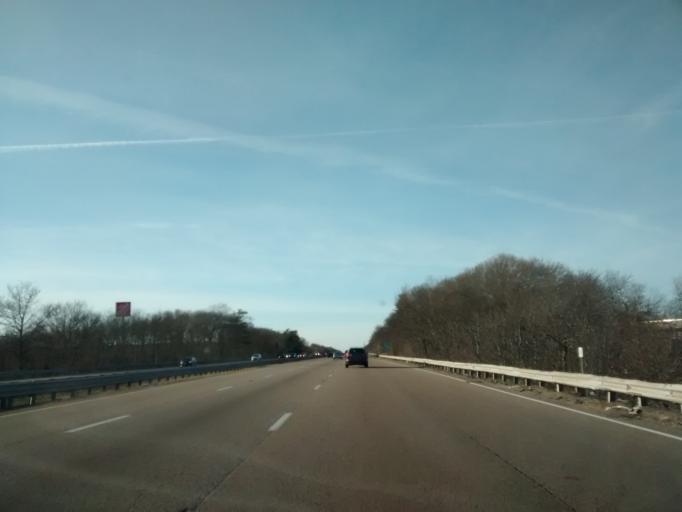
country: US
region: Massachusetts
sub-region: Norfolk County
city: Avon
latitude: 42.1287
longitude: -71.0628
